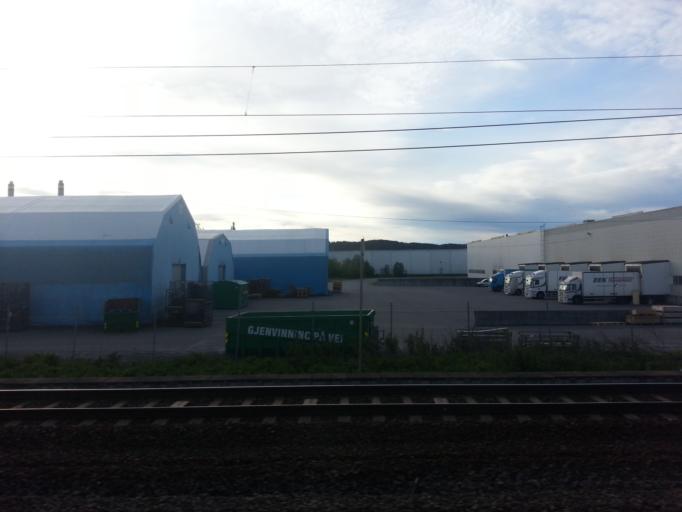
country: NO
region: Akershus
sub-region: Skedsmo
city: Lillestrom
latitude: 59.9708
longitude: 11.0687
